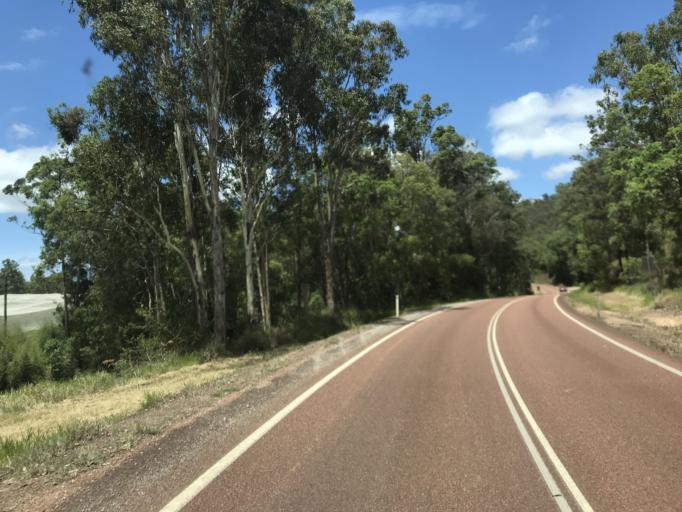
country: AU
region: Queensland
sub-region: Tablelands
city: Ravenshoe
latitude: -17.5992
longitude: 145.4773
